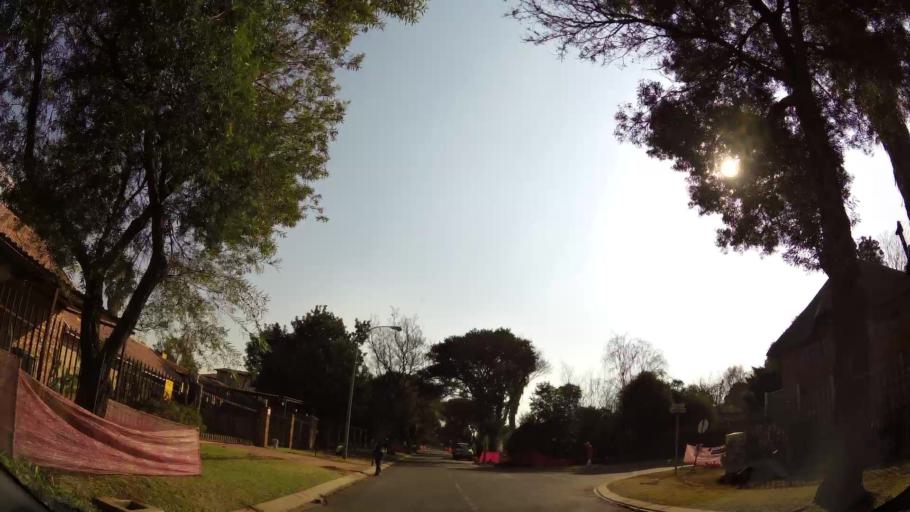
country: ZA
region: Gauteng
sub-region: Ekurhuleni Metropolitan Municipality
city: Benoni
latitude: -26.1555
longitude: 28.2862
